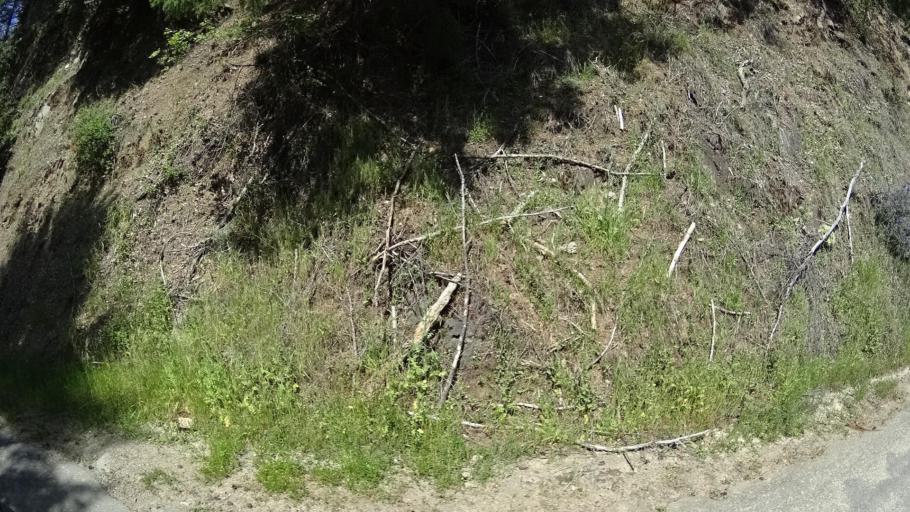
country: US
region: California
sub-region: Humboldt County
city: Redway
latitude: 40.1925
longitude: -123.5435
